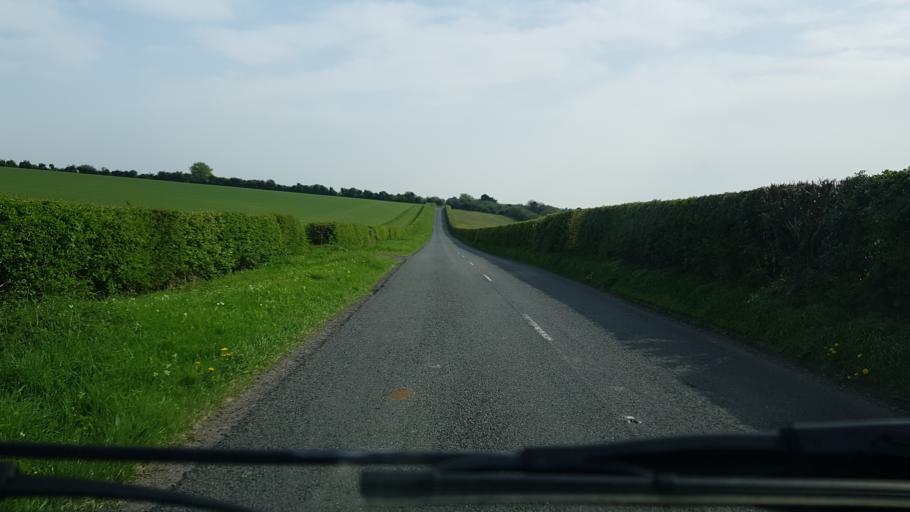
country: GB
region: England
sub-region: Hampshire
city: Overton
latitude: 51.2671
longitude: -1.2642
